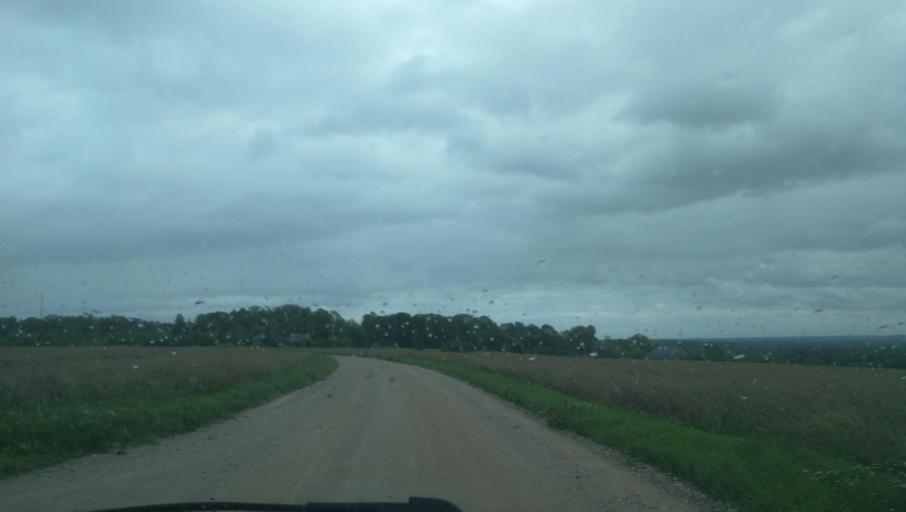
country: LV
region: Priekuli
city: Priekuli
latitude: 57.3669
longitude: 25.4300
